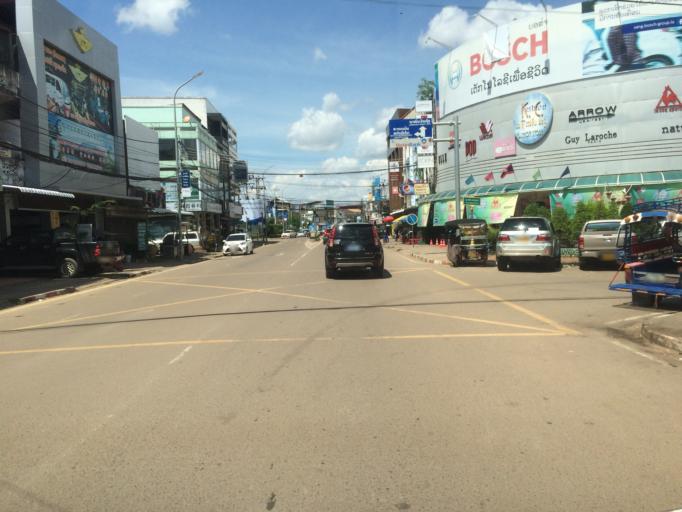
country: LA
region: Vientiane
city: Vientiane
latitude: 17.9679
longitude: 102.6027
